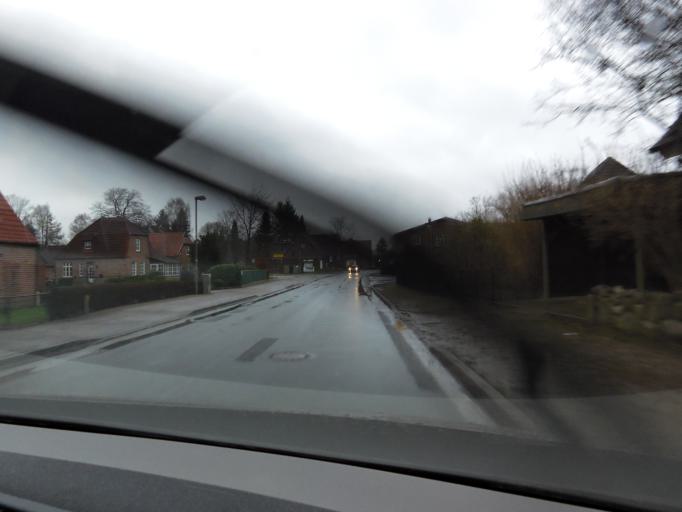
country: DE
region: Schleswig-Holstein
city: Schmilau
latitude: 53.6619
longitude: 10.7573
